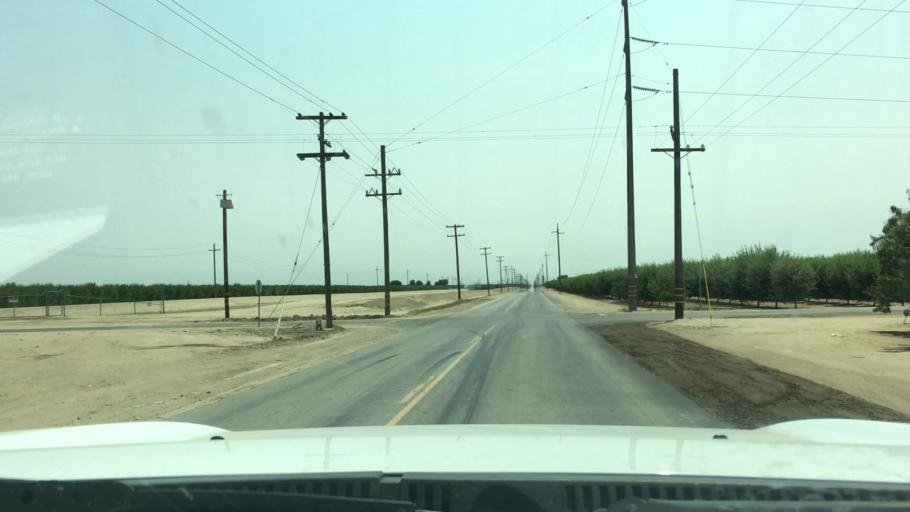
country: US
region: California
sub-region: Kern County
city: Wasco
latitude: 35.6163
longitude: -119.4379
